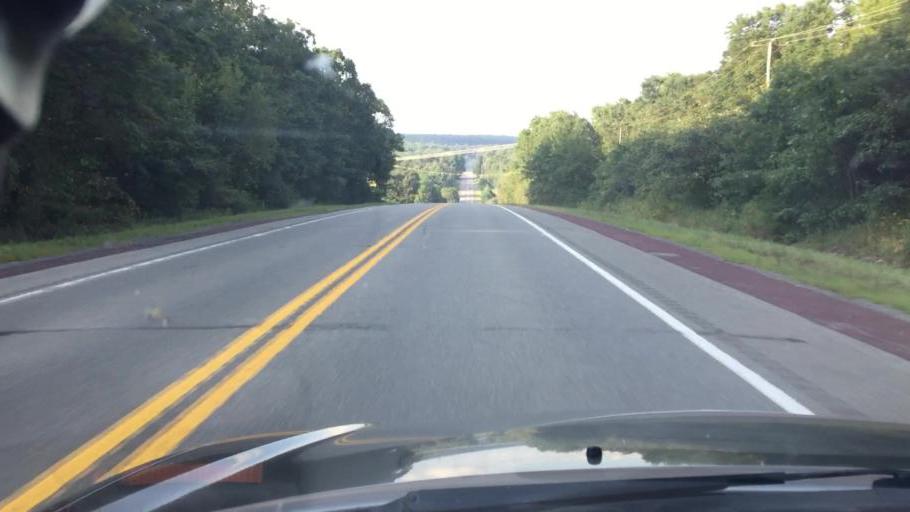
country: US
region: Pennsylvania
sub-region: Carbon County
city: Towamensing Trails
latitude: 40.9538
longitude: -75.6504
